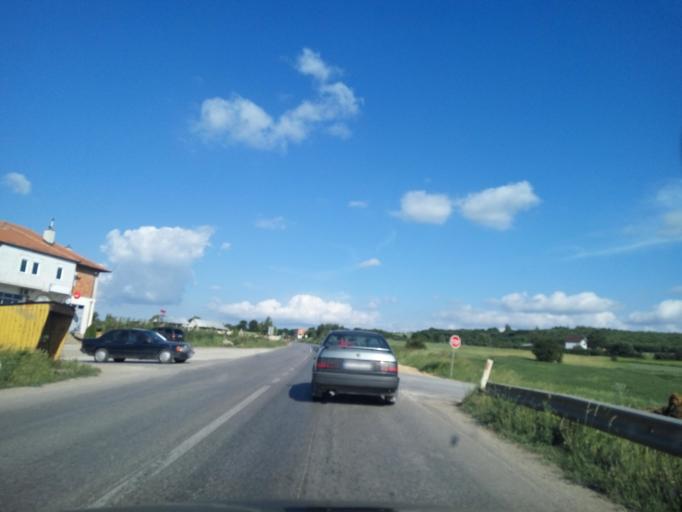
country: XK
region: Pec
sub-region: Komuna e Klines
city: Klina
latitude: 42.5885
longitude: 20.6701
